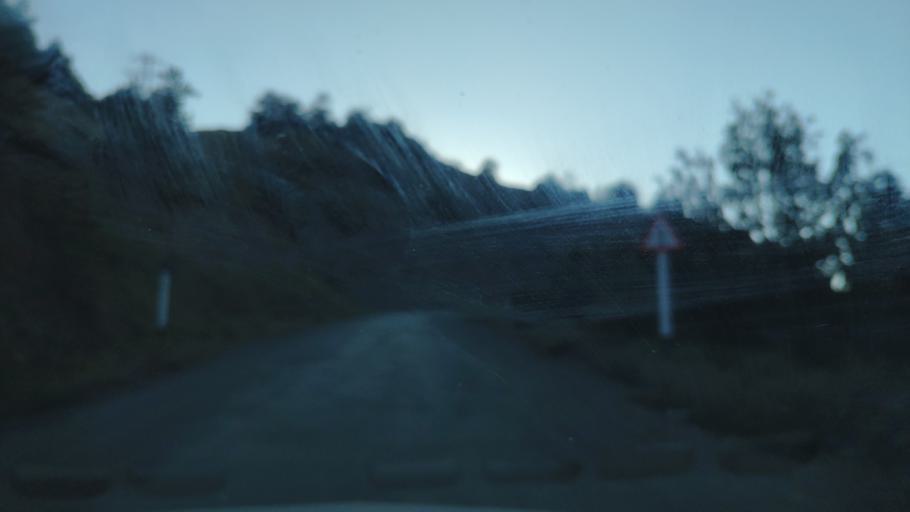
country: TJ
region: Viloyati Sughd
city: Ayni
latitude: 39.6401
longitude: 68.4725
